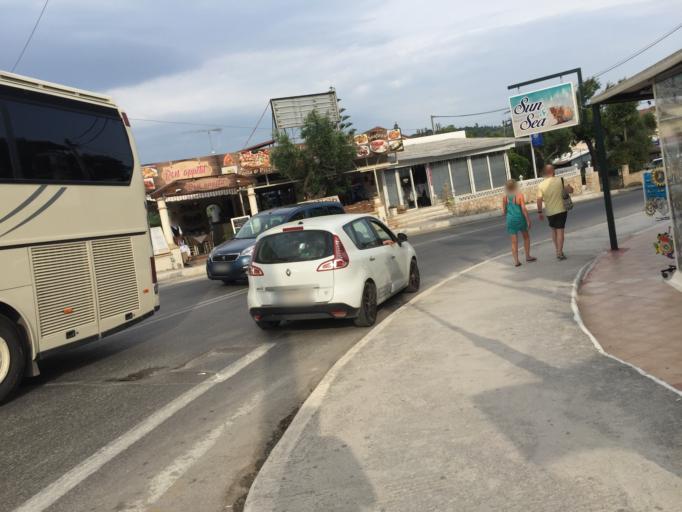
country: GR
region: Ionian Islands
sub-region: Nomos Zakynthou
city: Gaitanion
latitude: 37.8129
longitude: 20.8712
